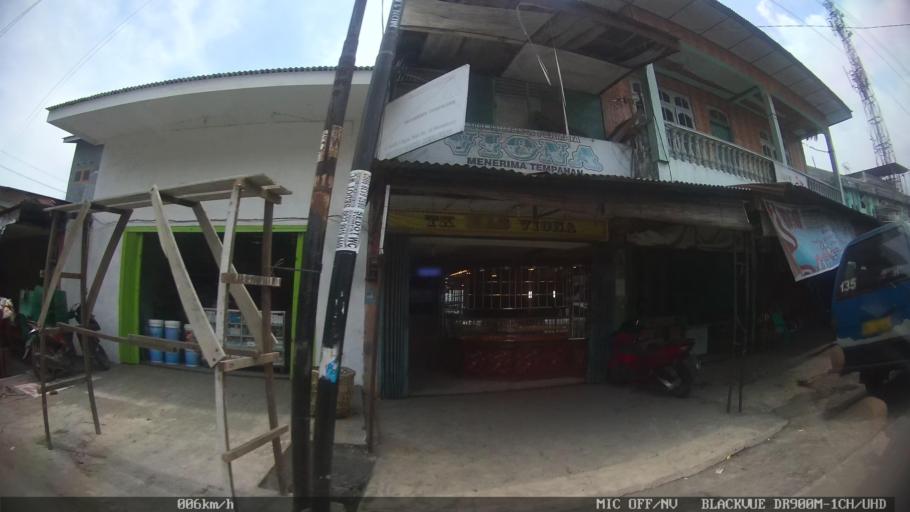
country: ID
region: North Sumatra
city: Labuhan Deli
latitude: 3.6859
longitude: 98.6911
